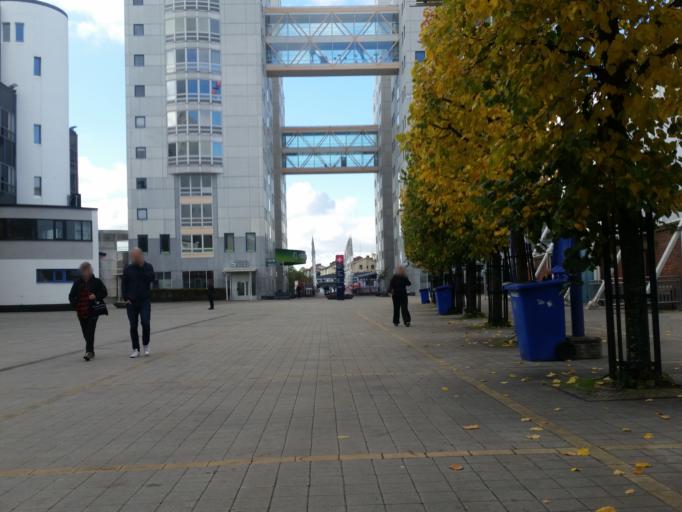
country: SE
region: Stockholm
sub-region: Stockholms Kommun
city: Arsta
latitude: 59.2943
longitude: 18.0819
